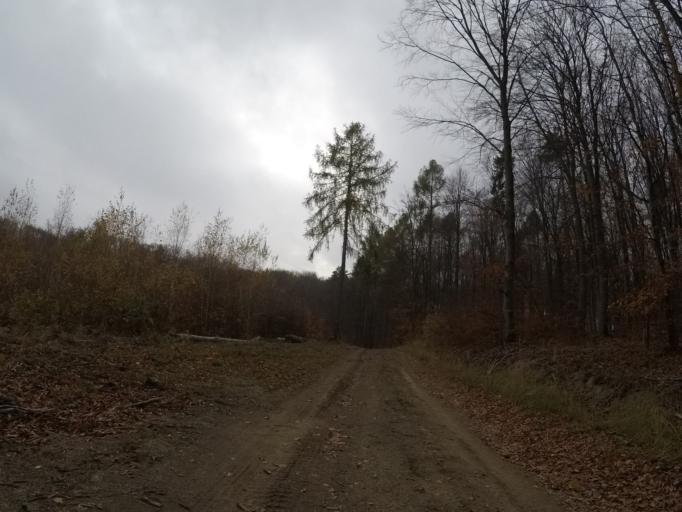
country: SK
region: Presovsky
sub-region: Okres Presov
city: Presov
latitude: 48.8889
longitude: 21.1714
